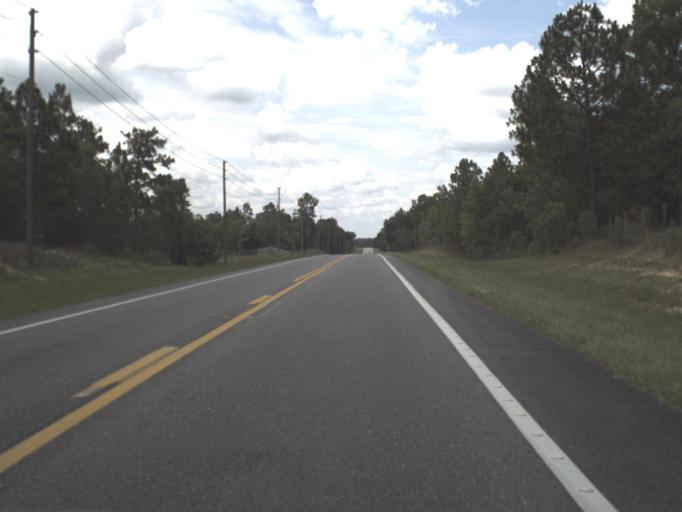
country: US
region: Florida
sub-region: Levy County
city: Williston Highlands
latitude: 29.3537
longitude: -82.5067
